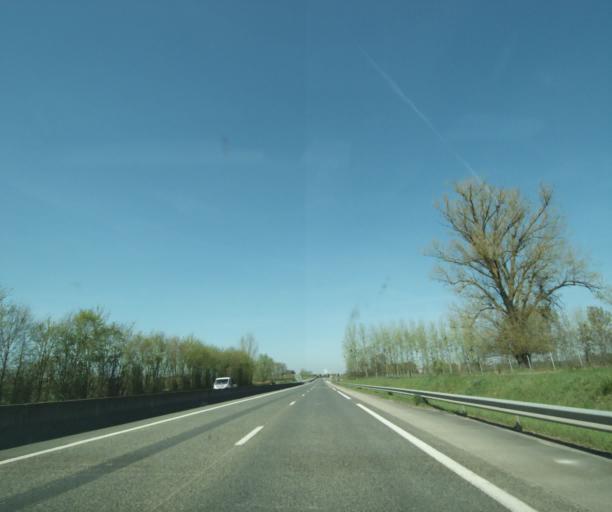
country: FR
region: Auvergne
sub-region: Departement de l'Allier
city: Avermes
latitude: 46.5947
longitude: 3.3147
